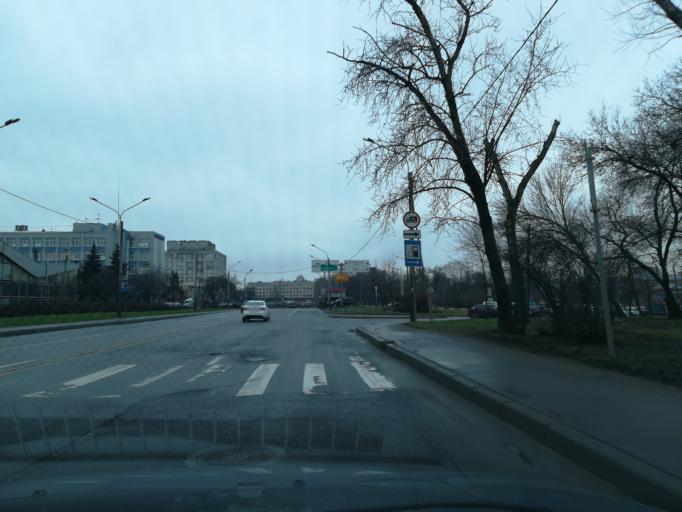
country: RU
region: St.-Petersburg
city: Avtovo
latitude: 59.8606
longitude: 30.2600
